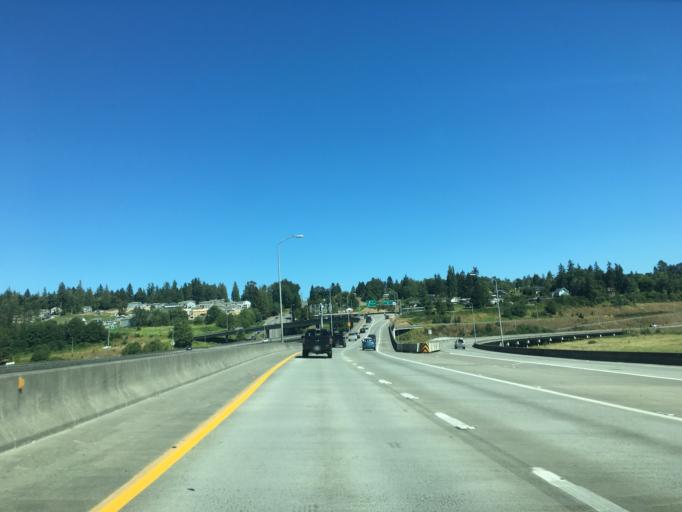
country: US
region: Washington
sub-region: Snohomish County
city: Fobes Hill
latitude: 47.9781
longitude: -122.1431
